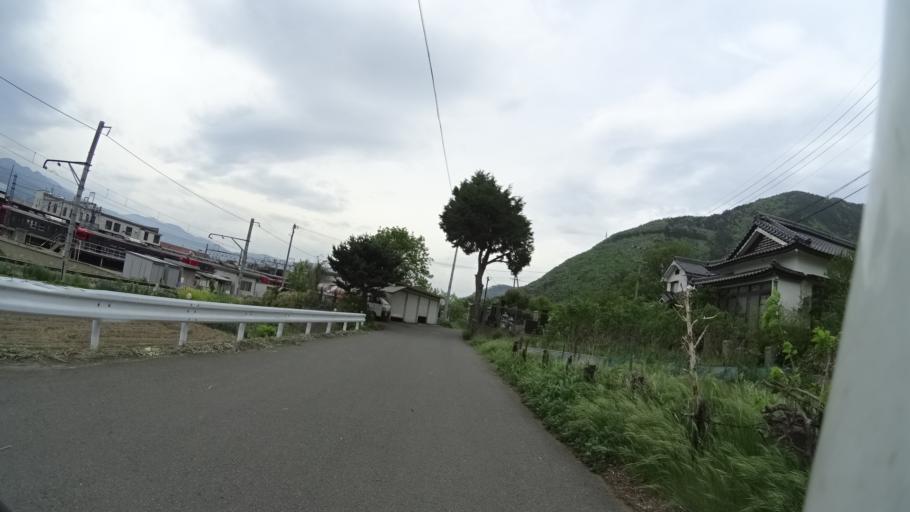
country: JP
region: Nagano
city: Ueda
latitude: 36.4925
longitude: 138.1541
